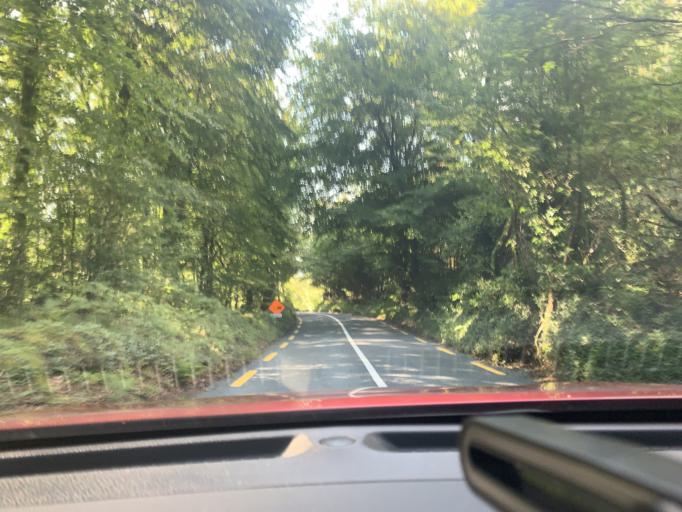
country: IE
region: Connaught
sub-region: Sligo
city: Strandhill
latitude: 54.1975
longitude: -8.5857
